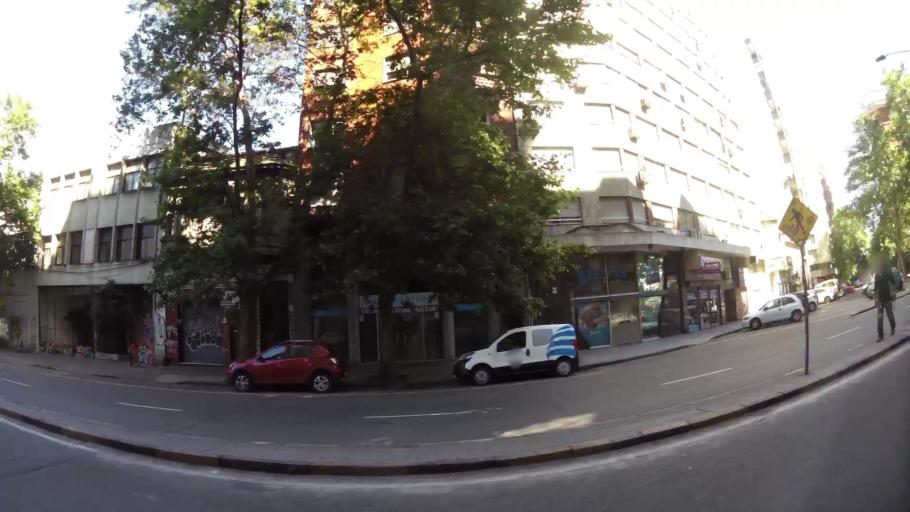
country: UY
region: Montevideo
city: Montevideo
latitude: -34.8973
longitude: -56.1663
